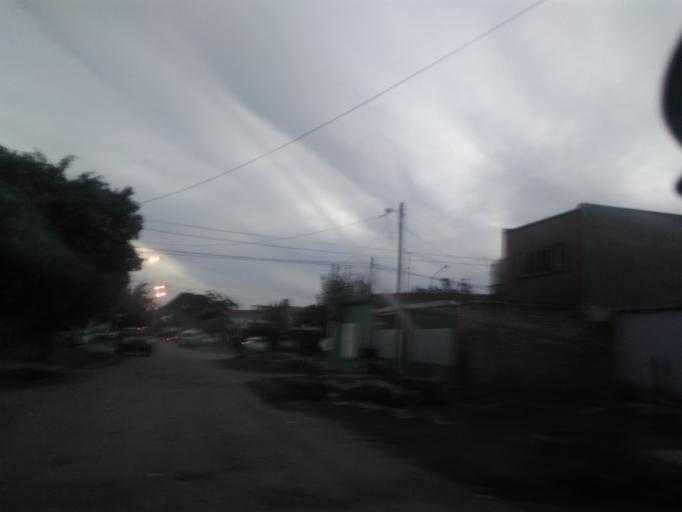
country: AR
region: Chaco
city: Resistencia
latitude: -27.4326
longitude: -58.9962
